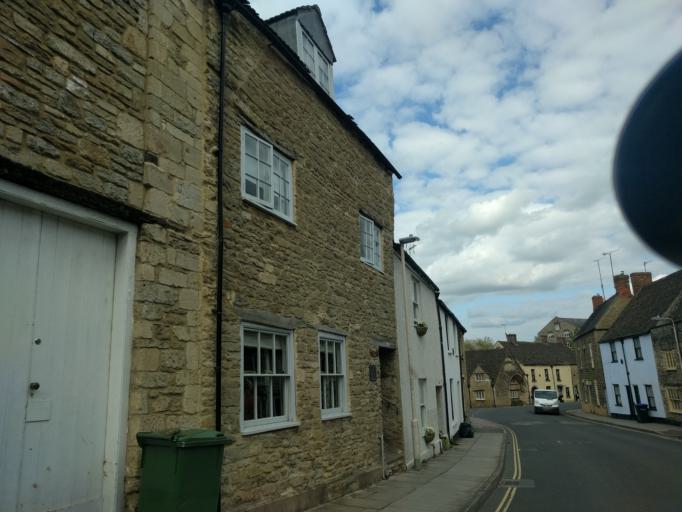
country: GB
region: England
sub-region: Wiltshire
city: Malmesbury
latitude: 51.5812
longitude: -2.0959
